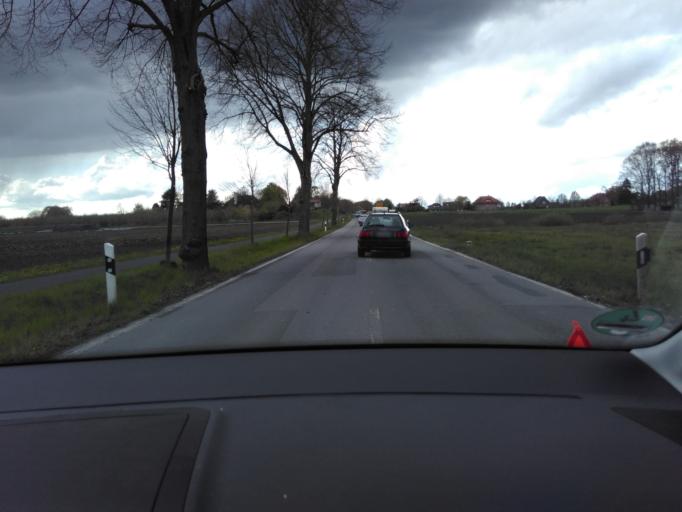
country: DE
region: North Rhine-Westphalia
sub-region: Regierungsbezirk Detmold
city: Verl
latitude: 51.9157
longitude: 8.4553
